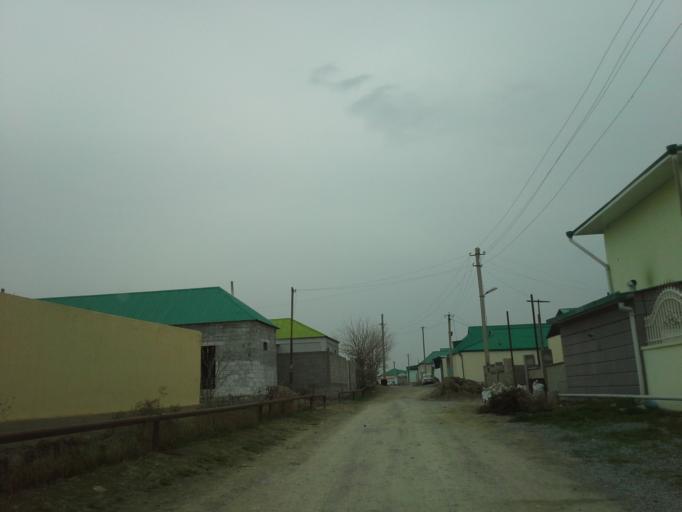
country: TM
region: Ahal
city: Abadan
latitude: 37.9788
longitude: 58.2232
